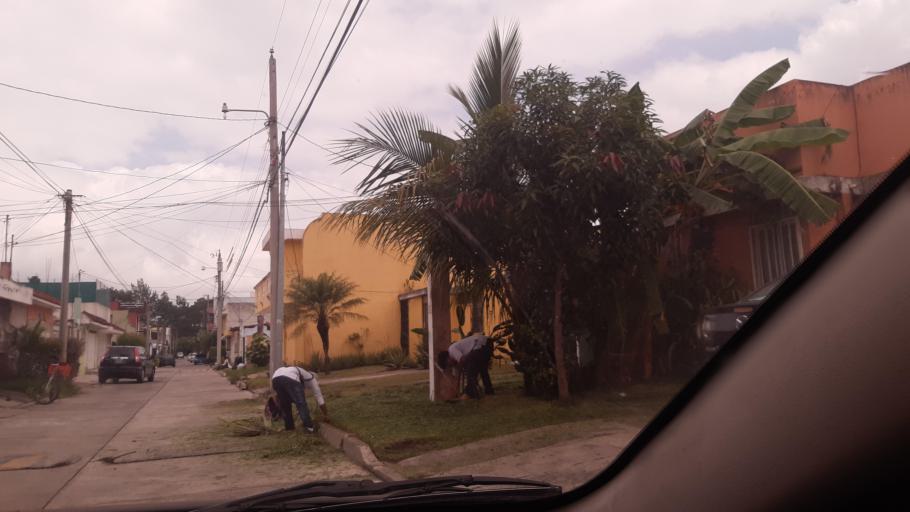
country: GT
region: Guatemala
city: Petapa
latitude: 14.5067
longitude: -90.5447
